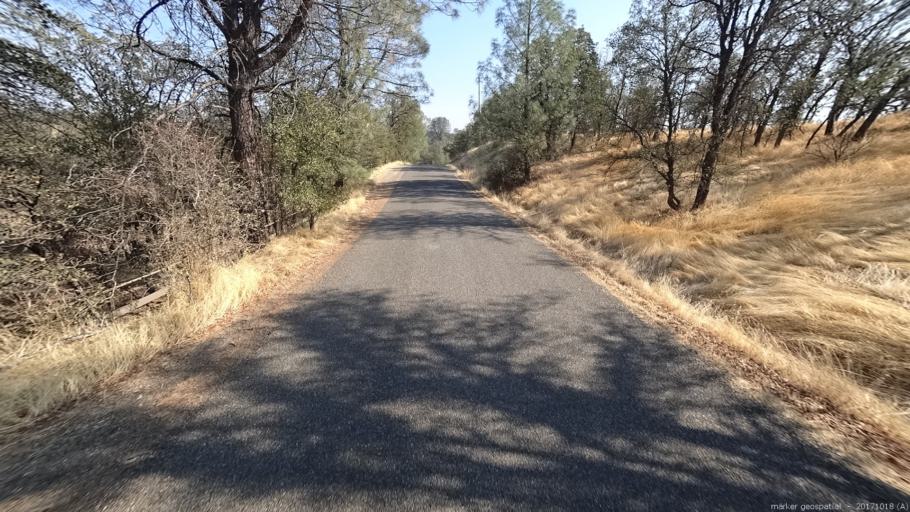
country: US
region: California
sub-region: Shasta County
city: Palo Cedro
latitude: 40.5562
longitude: -122.2529
